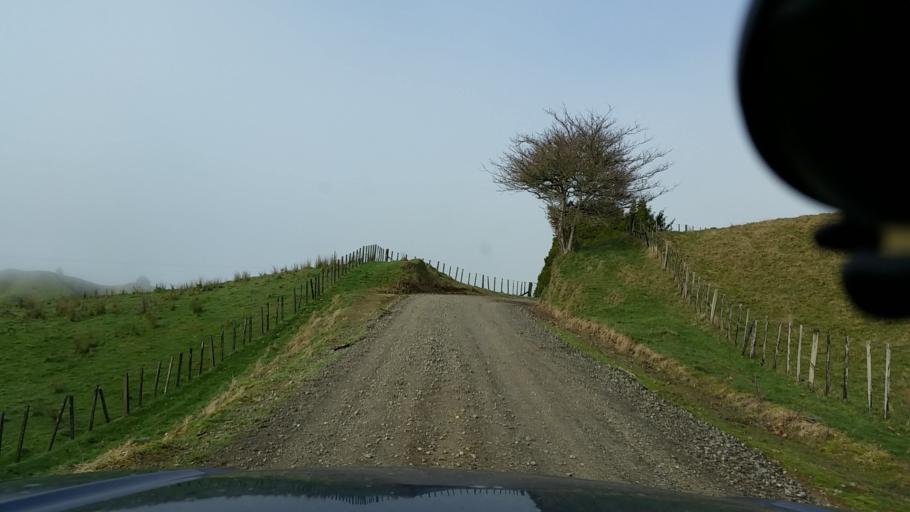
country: NZ
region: Taranaki
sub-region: New Plymouth District
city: Waitara
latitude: -39.0002
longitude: 174.7675
